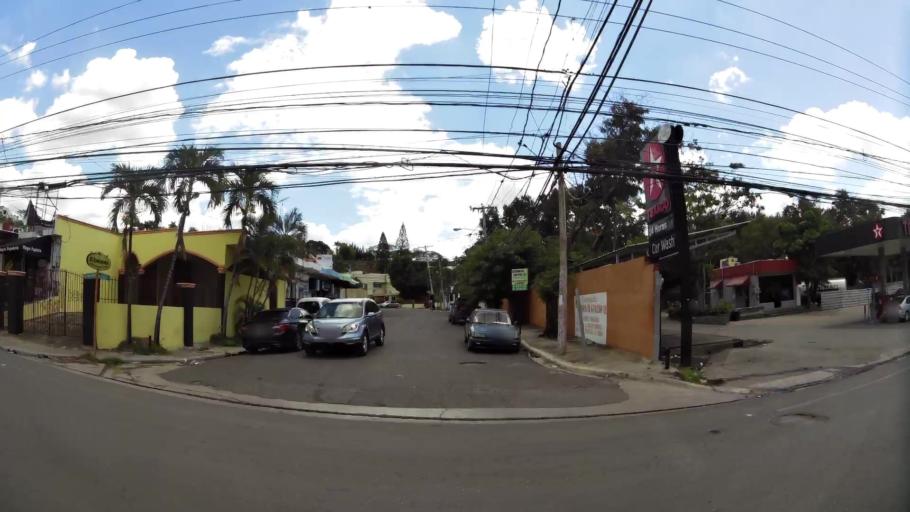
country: DO
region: Santiago
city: Santiago de los Caballeros
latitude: 19.4691
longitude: -70.6857
